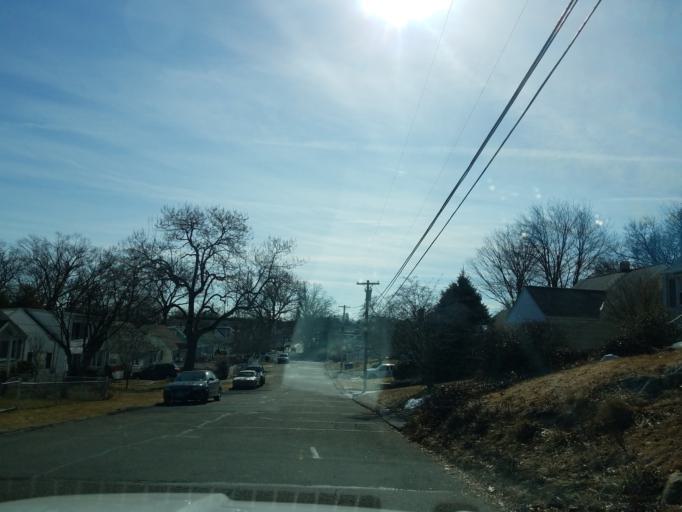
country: US
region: Connecticut
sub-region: Fairfield County
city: Norwalk
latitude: 41.1103
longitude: -73.4313
